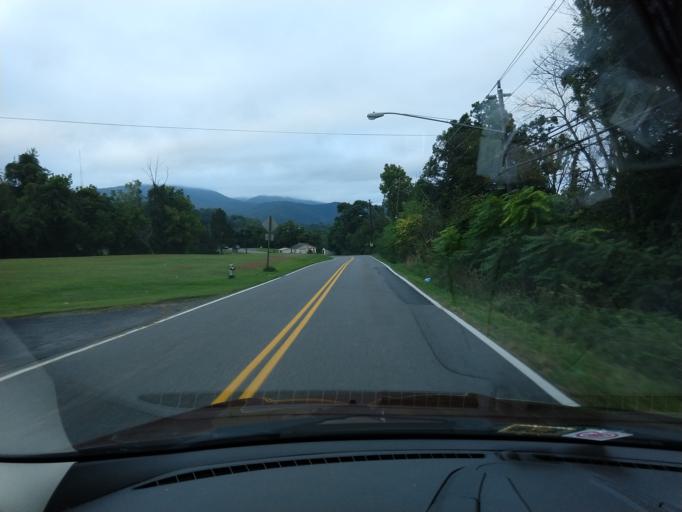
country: US
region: Virginia
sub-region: City of Covington
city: Fairlawn
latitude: 37.7763
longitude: -79.9857
